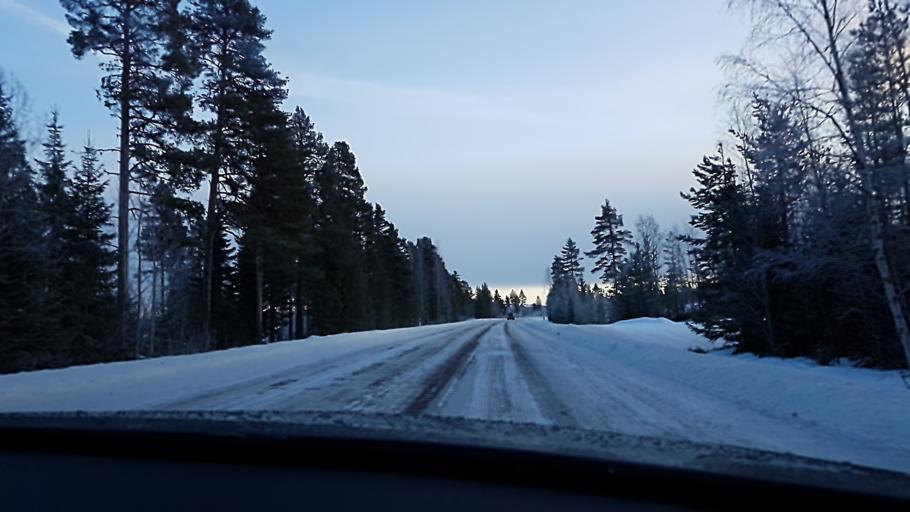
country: SE
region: Jaemtland
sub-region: Bergs Kommun
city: Hoverberg
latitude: 62.4913
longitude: 14.4786
